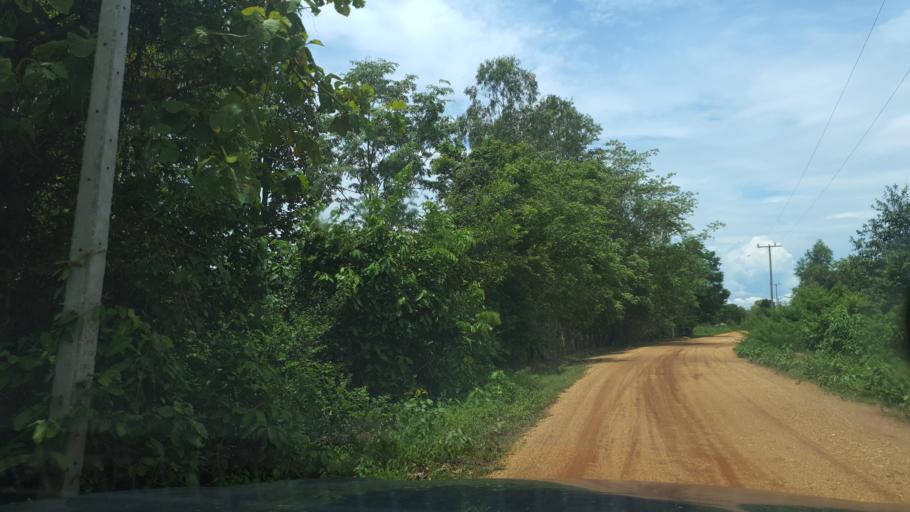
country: TH
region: Lampang
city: Ko Kha
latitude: 18.1849
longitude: 99.3172
